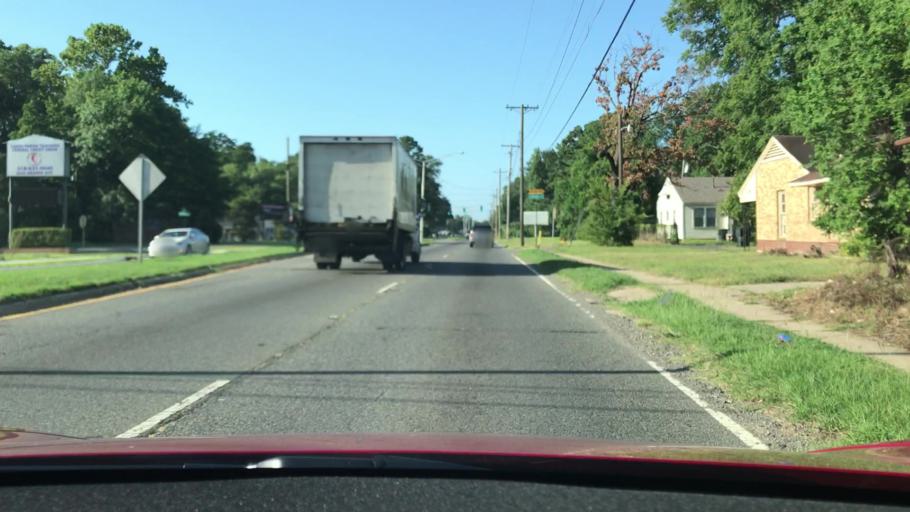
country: US
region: Louisiana
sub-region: Caddo Parish
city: Shreveport
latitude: 32.4678
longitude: -93.7801
